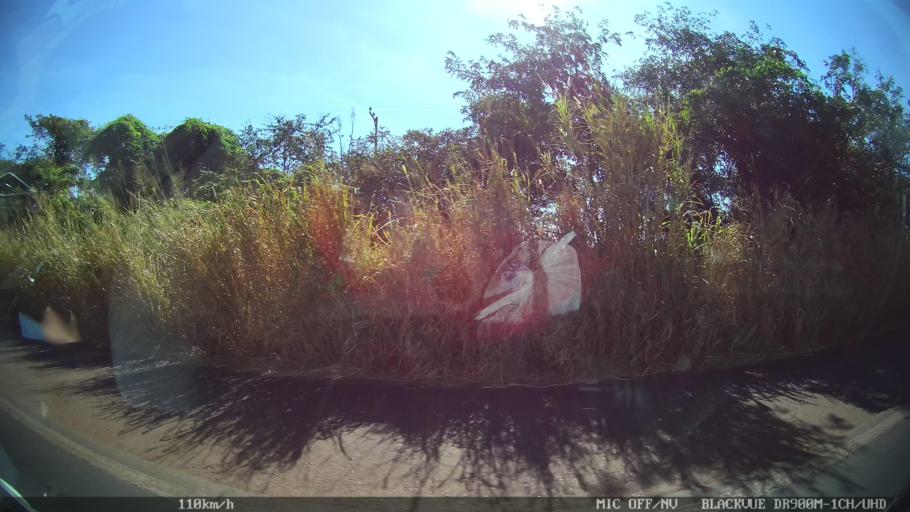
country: BR
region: Sao Paulo
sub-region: Barretos
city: Barretos
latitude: -20.4805
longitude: -48.5035
